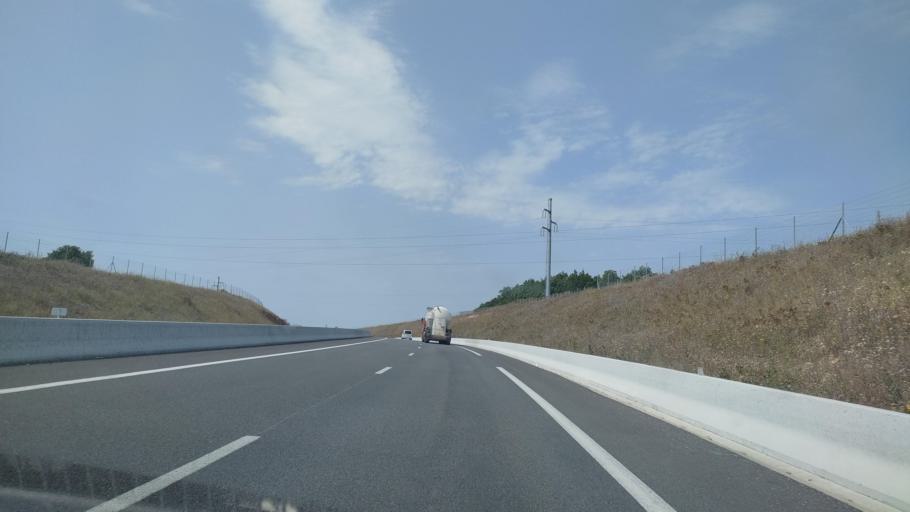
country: FR
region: Poitou-Charentes
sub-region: Departement de la Charente
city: Balzac
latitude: 45.6937
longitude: 0.0896
